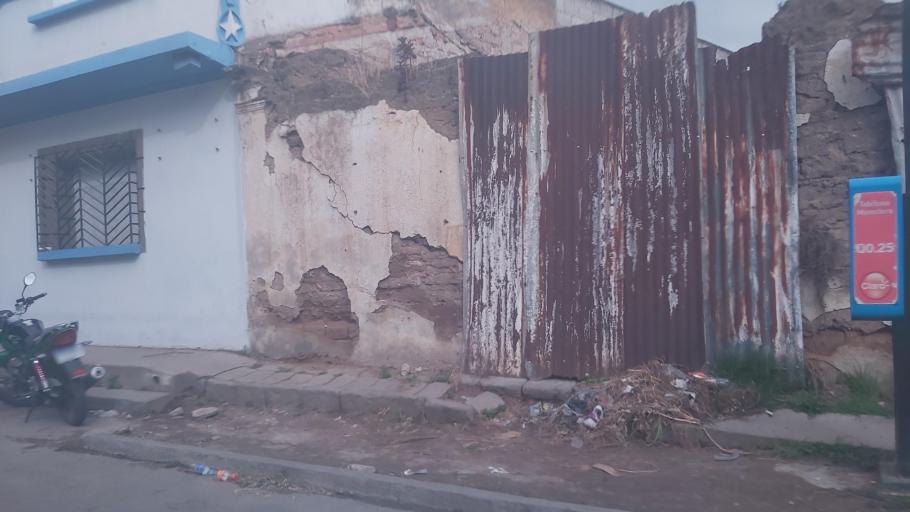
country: GT
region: Quetzaltenango
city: Quetzaltenango
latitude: 14.8314
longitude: -91.5217
